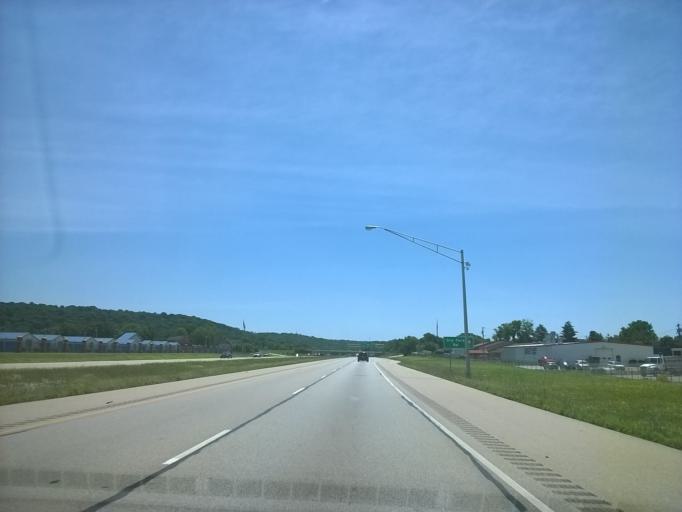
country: US
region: Ohio
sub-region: Hamilton County
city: Harrison
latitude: 39.2443
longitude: -84.7779
